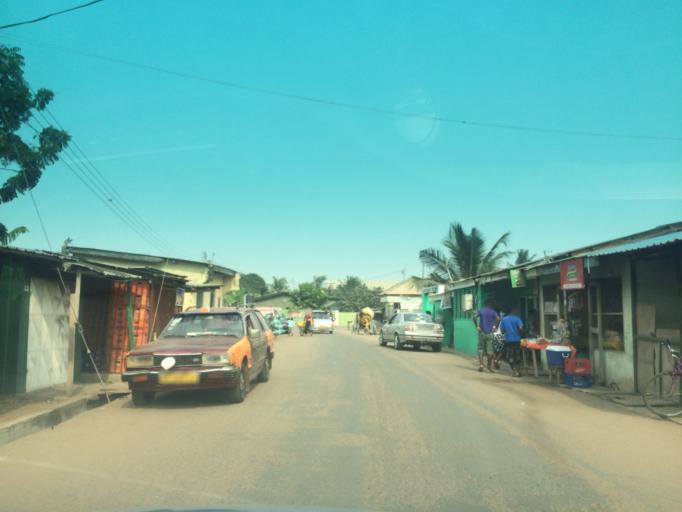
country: GH
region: Greater Accra
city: Nungua
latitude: 5.6047
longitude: -0.0870
